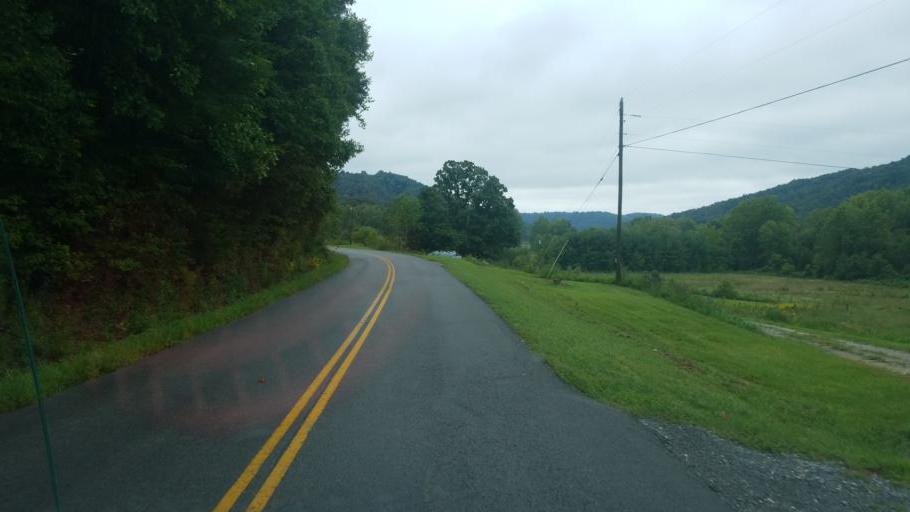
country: US
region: Kentucky
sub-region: Fleming County
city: Flemingsburg
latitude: 38.3727
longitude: -83.5383
